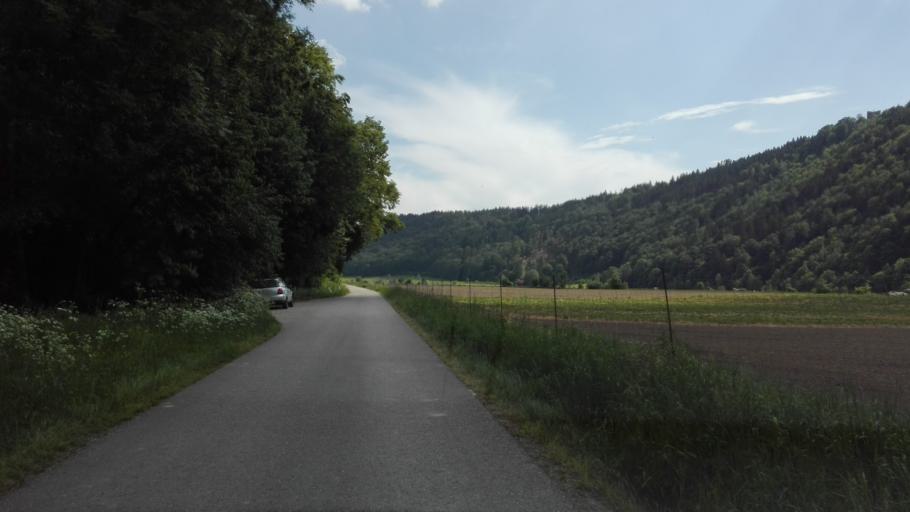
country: AT
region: Upper Austria
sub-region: Politischer Bezirk Rohrbach
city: Pfarrkirchen im Muehlkreis
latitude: 48.4436
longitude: 13.8575
